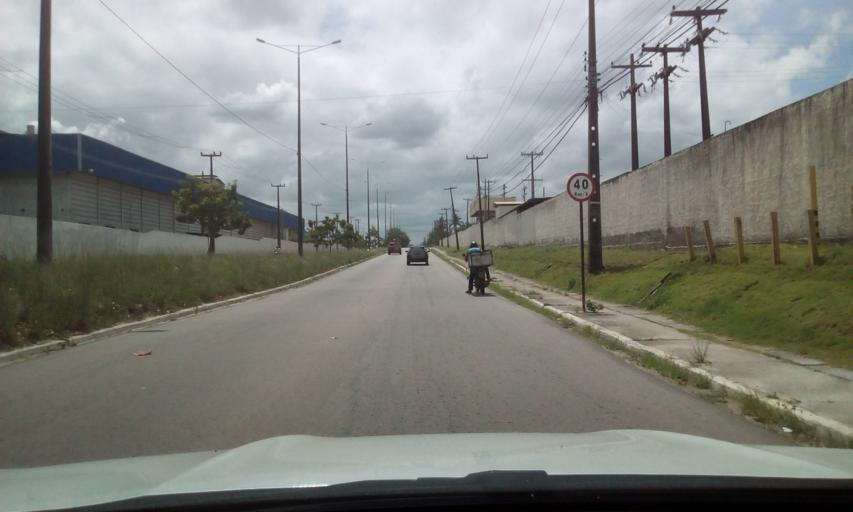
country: BR
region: Paraiba
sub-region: Bayeux
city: Bayeux
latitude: -7.1785
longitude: -34.9062
